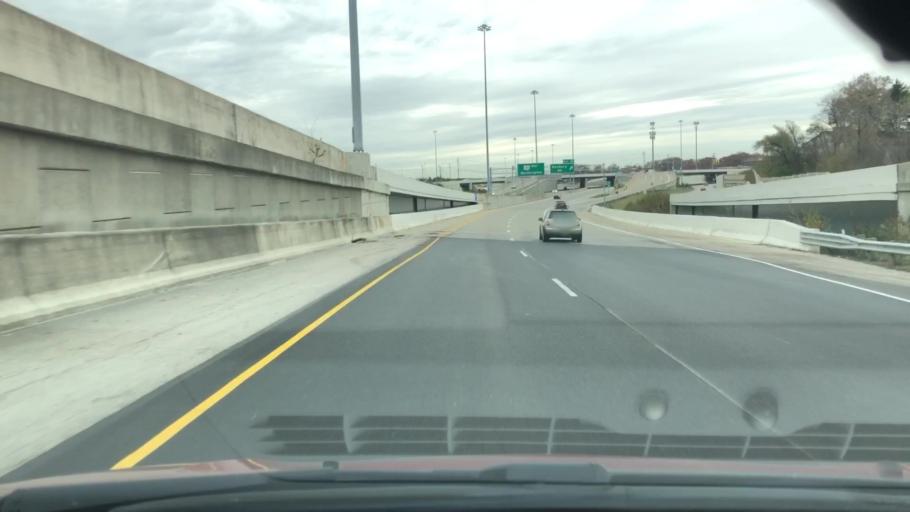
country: US
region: Ohio
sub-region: Franklin County
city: Huber Ridge
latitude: 40.0804
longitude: -82.8902
